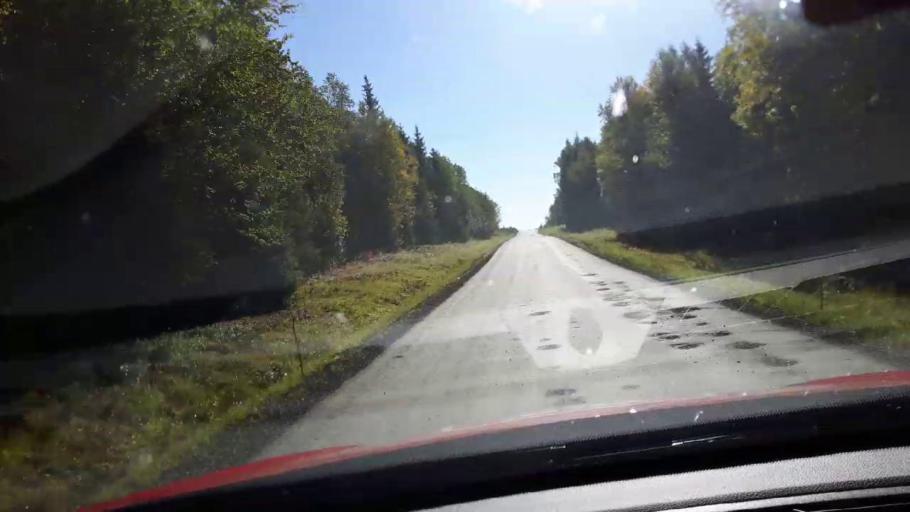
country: NO
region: Nord-Trondelag
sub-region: Lierne
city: Sandvika
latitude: 64.6045
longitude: 13.9651
